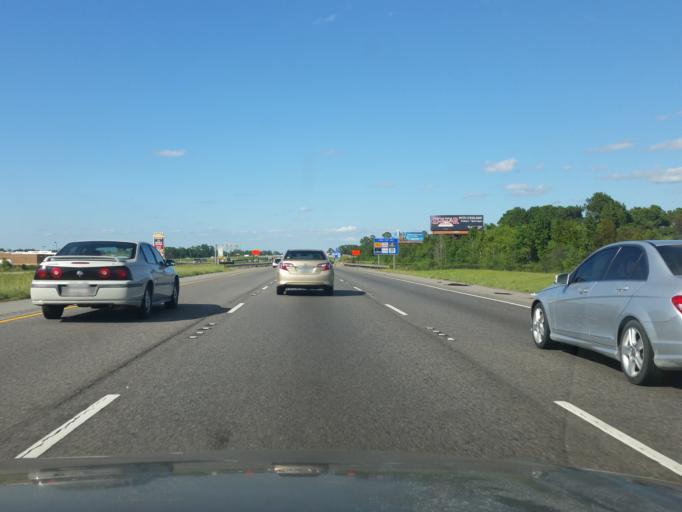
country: US
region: Louisiana
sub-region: Saint Tammany Parish
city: Slidell
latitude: 30.2608
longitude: -89.7585
